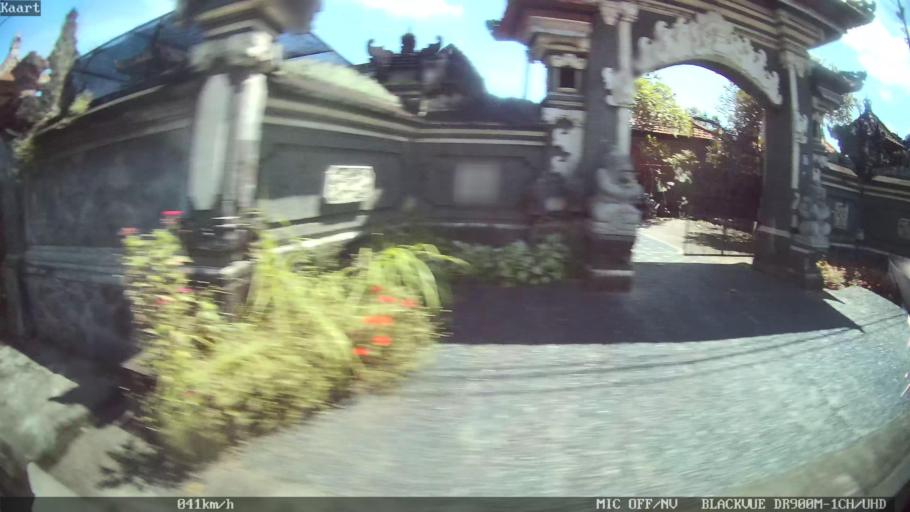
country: ID
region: Bali
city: Banjar Kelodan
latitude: -8.5470
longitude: 115.3346
